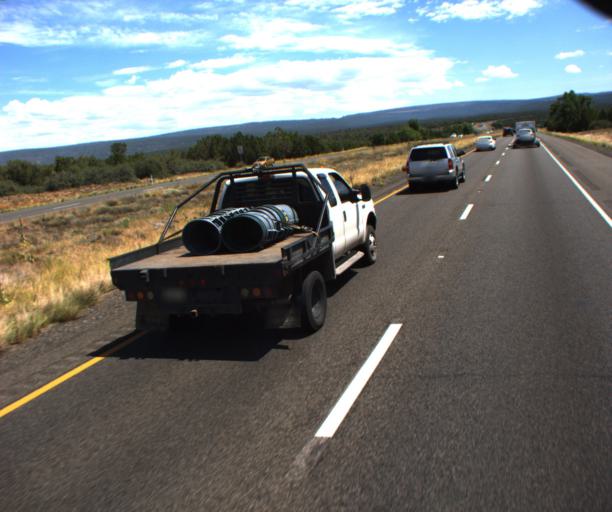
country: US
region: Arizona
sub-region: Yavapai County
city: Village of Oak Creek (Big Park)
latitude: 34.7582
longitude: -111.6645
